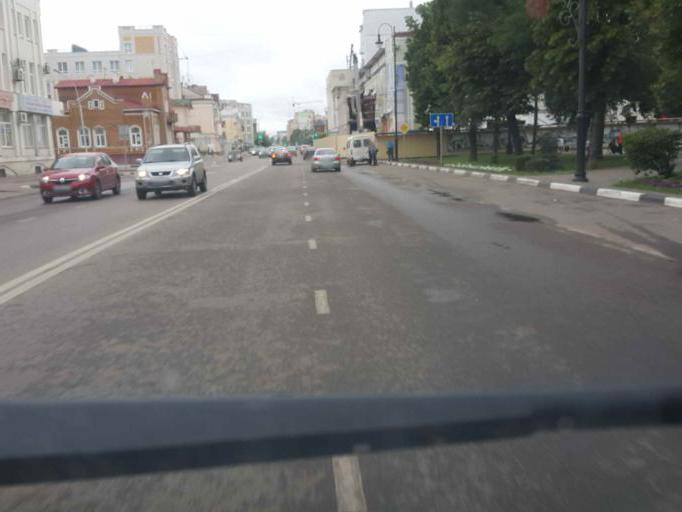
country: RU
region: Tambov
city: Tambov
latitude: 52.7239
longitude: 41.4513
